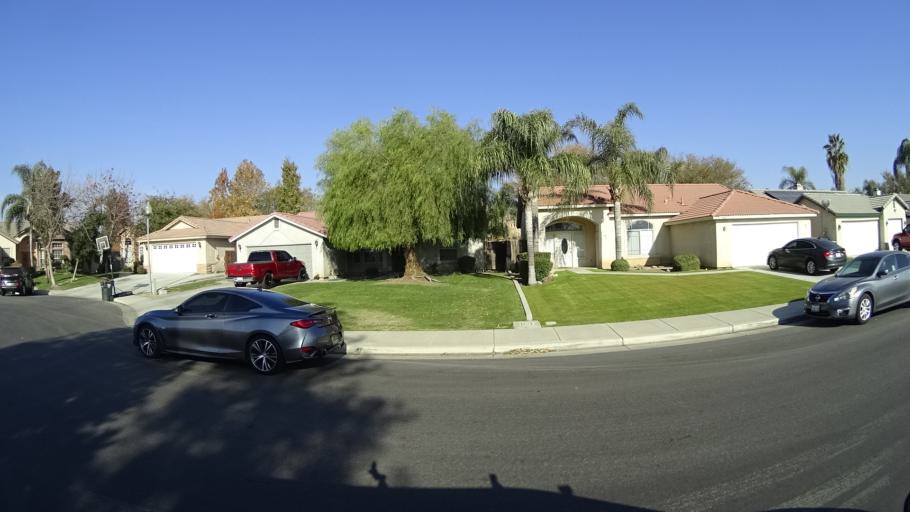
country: US
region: California
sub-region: Kern County
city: Greenacres
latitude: 35.3680
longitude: -119.1093
